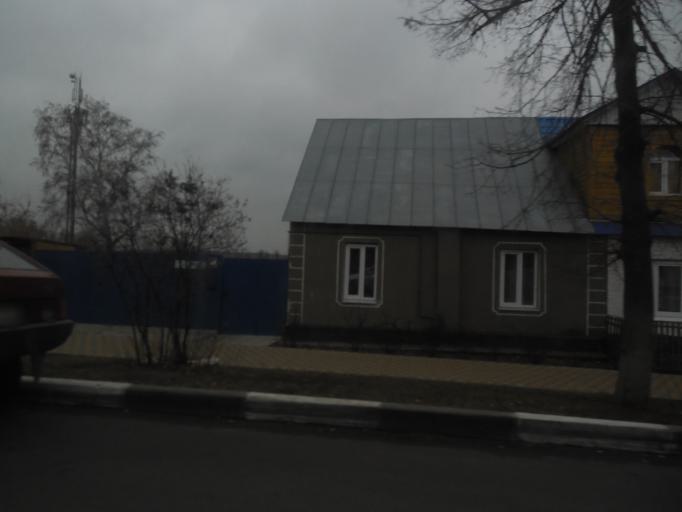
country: RU
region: Lipetsk
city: Zadonsk
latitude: 52.3919
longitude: 38.9261
